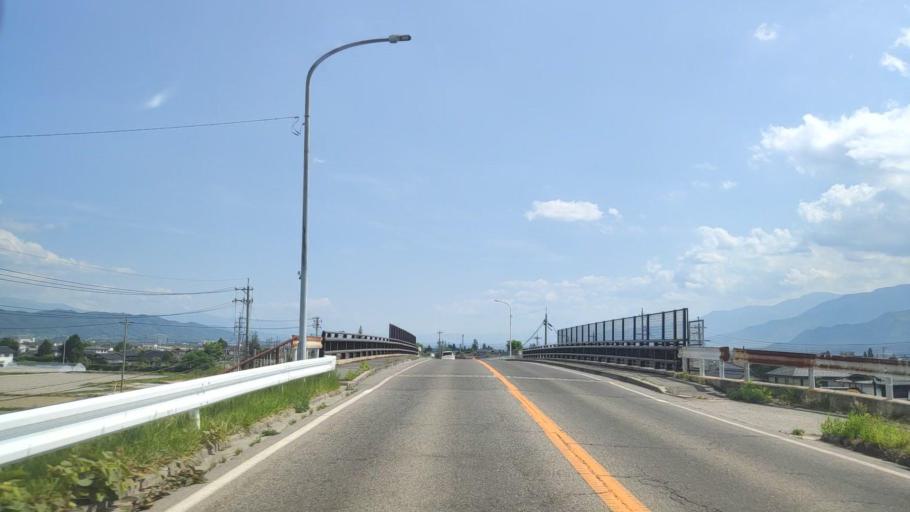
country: JP
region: Nagano
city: Omachi
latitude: 36.4513
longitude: 137.8523
